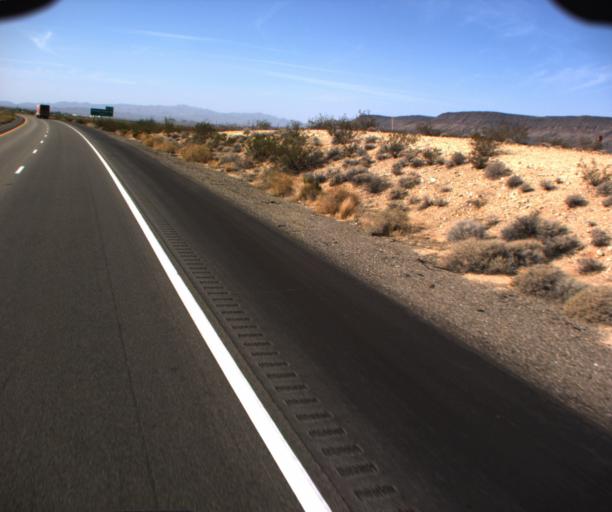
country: US
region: Arizona
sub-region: Mohave County
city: Kingman
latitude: 34.8975
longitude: -114.1553
